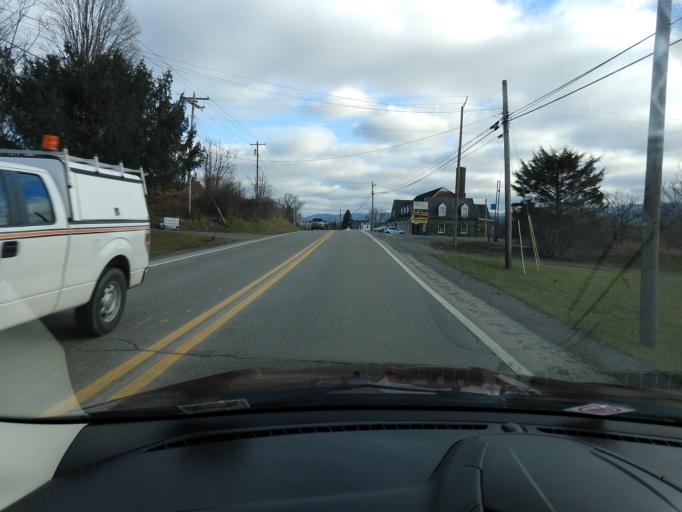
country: US
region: West Virginia
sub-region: Randolph County
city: Elkins
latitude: 38.7956
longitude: -79.9003
